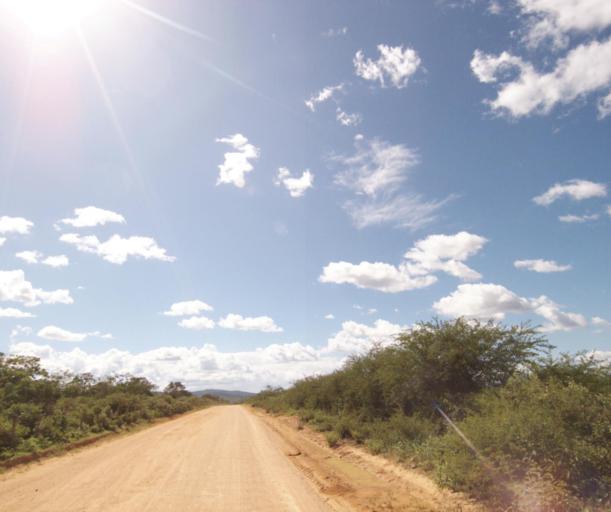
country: BR
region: Bahia
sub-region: Pocoes
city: Pocoes
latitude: -14.2484
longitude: -40.7499
